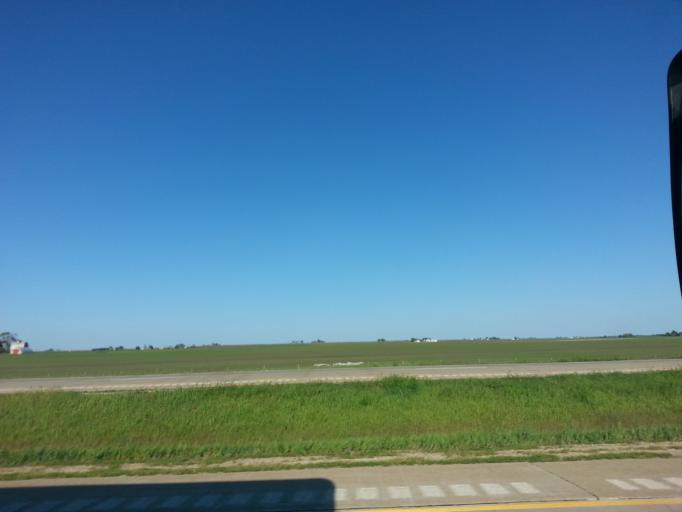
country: US
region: Illinois
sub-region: Woodford County
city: El Paso
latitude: 40.7194
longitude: -89.0342
